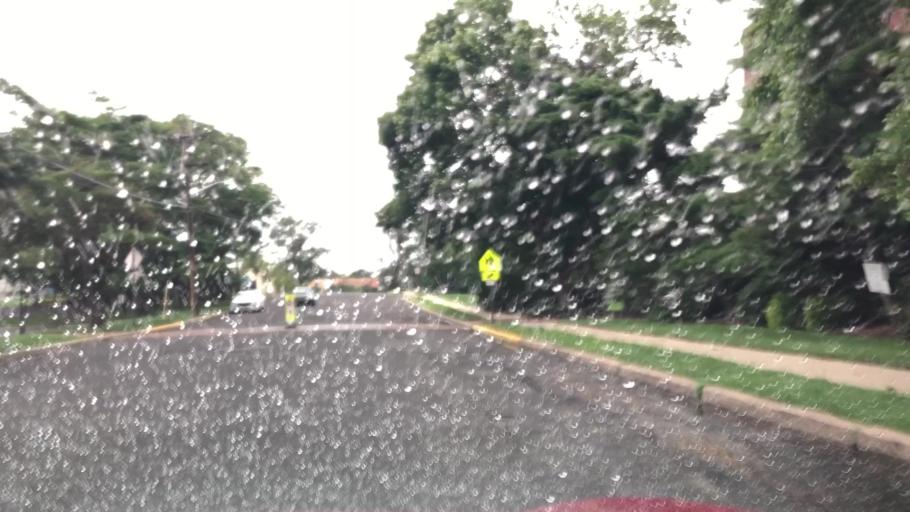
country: US
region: New Jersey
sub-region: Bergen County
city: Hackensack
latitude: 40.8977
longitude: -74.0347
